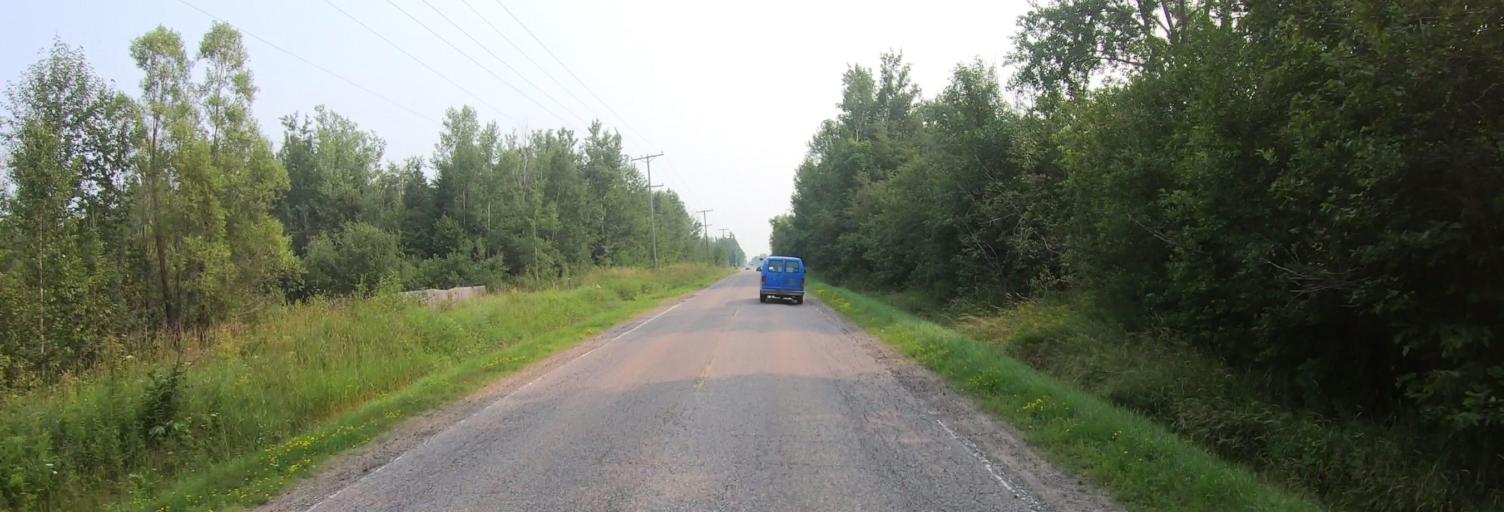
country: US
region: Michigan
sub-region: Chippewa County
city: Sault Ste. Marie
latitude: 46.4656
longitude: -84.3013
